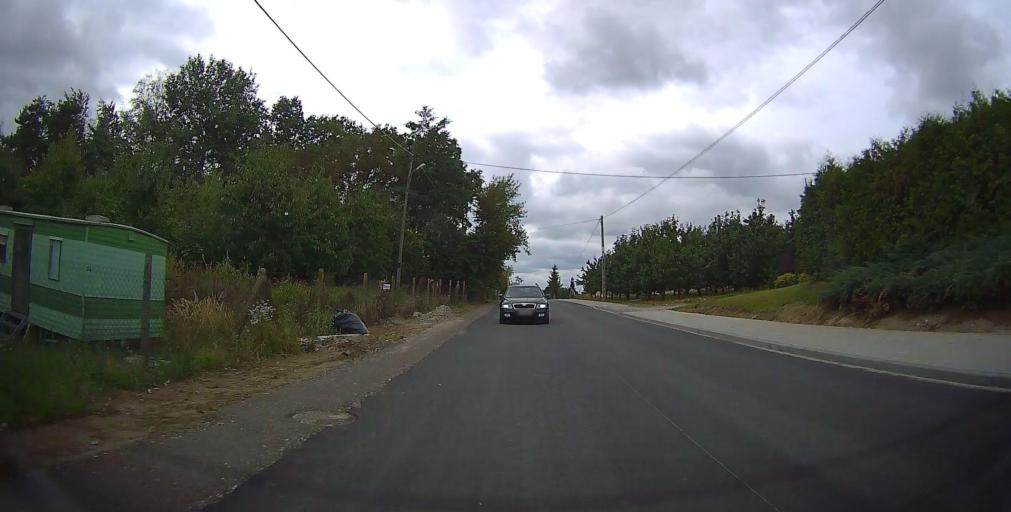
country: PL
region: Masovian Voivodeship
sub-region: Powiat grojecki
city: Belsk Duzy
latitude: 51.8136
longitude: 20.8319
